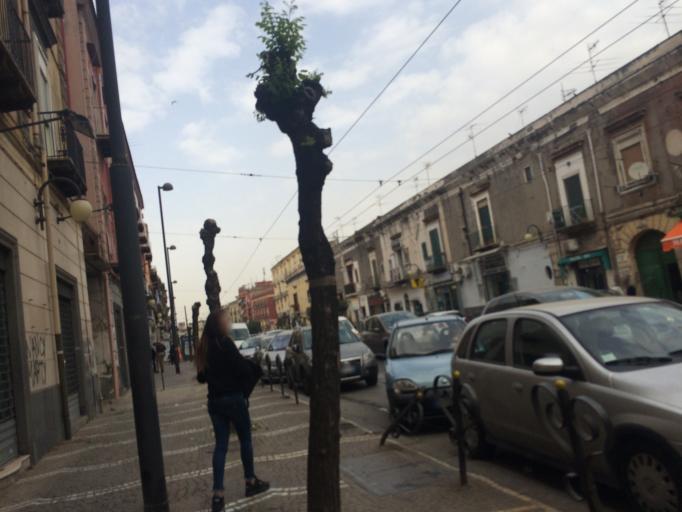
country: IT
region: Campania
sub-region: Provincia di Napoli
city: San Giorgio a Cremano
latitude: 40.8355
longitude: 14.3039
